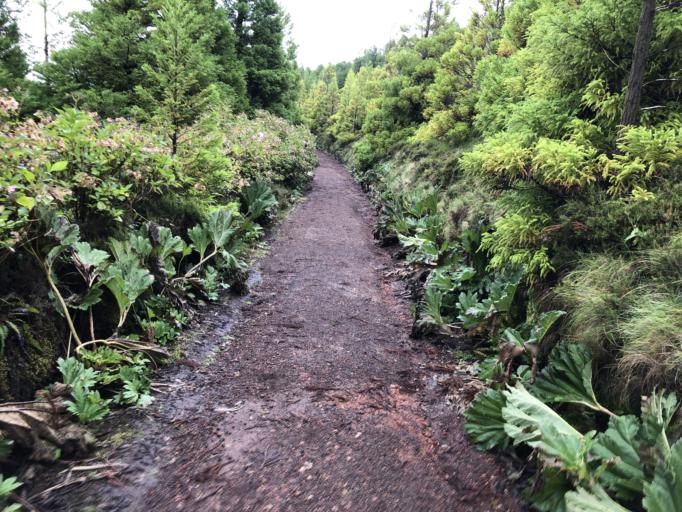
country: PT
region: Azores
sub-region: Ponta Delgada
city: Arrifes
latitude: 37.8250
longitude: -25.7498
